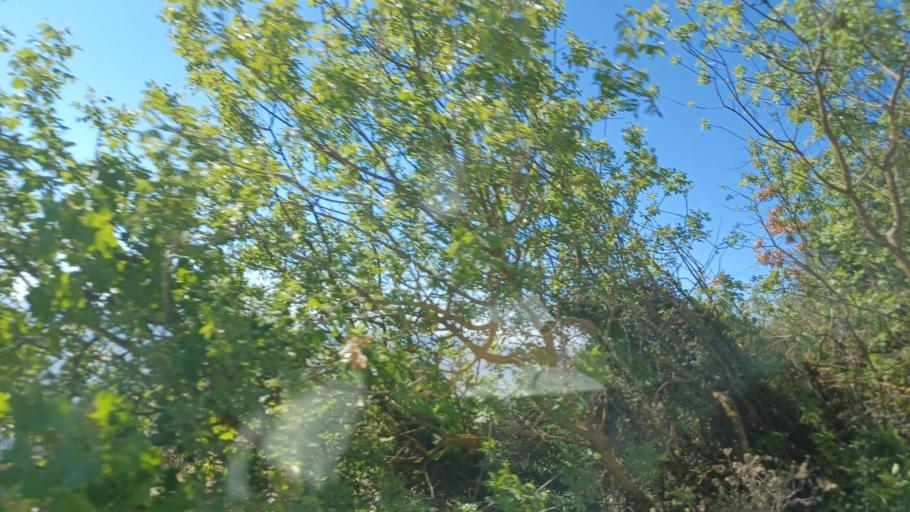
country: CY
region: Pafos
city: Mesogi
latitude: 34.8918
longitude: 32.6265
